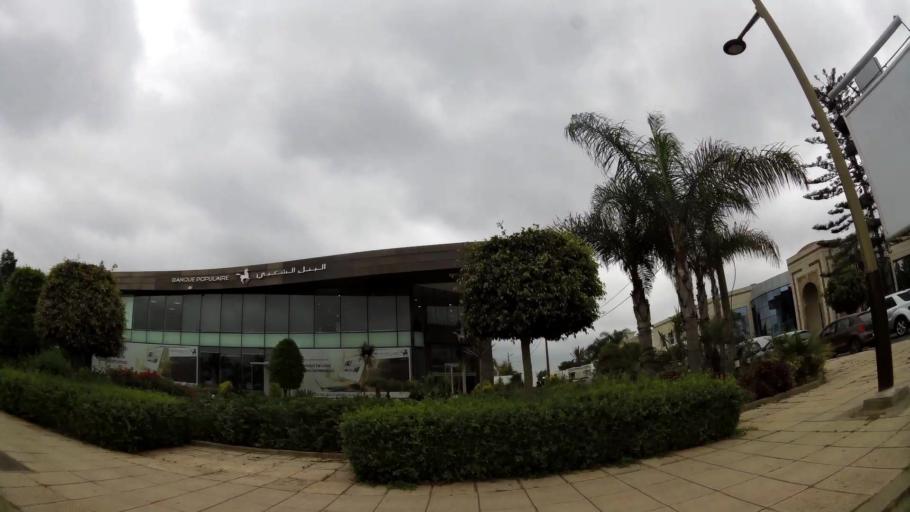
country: MA
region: Rabat-Sale-Zemmour-Zaer
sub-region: Rabat
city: Rabat
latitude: 33.9713
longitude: -6.8291
